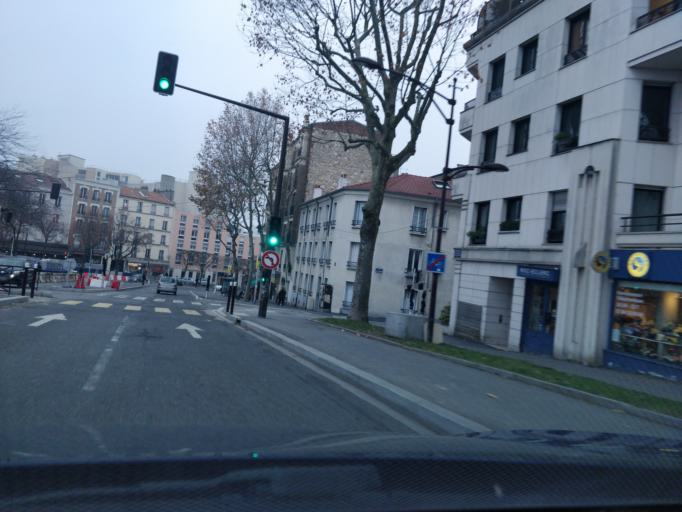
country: FR
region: Ile-de-France
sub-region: Departement du Val-de-Marne
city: Le Kremlin-Bicetre
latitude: 48.8091
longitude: 2.3582
